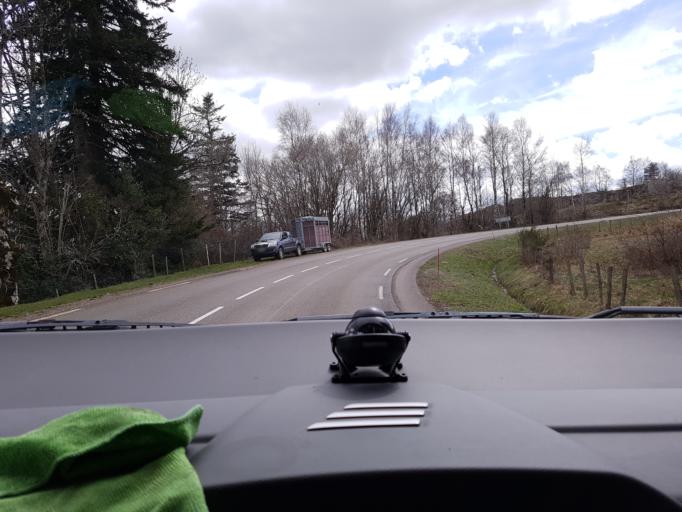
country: FR
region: Midi-Pyrenees
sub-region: Departement de l'Aveyron
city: Laguiole
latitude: 44.7772
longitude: 2.8977
